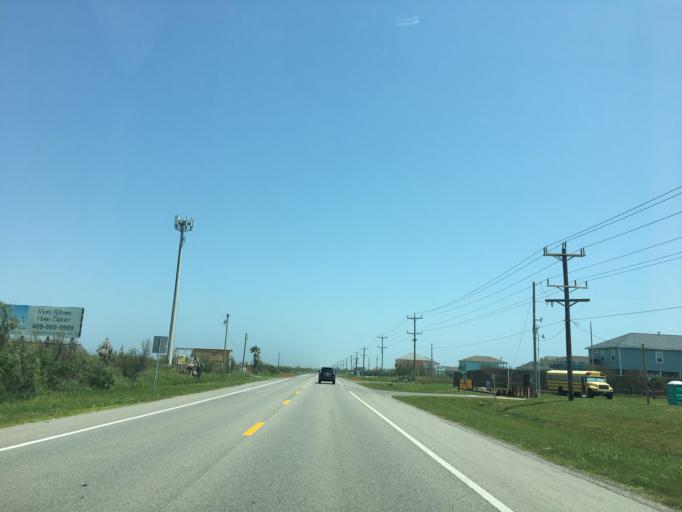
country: US
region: Texas
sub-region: Galveston County
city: Bolivar Peninsula
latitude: 29.4936
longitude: -94.5407
